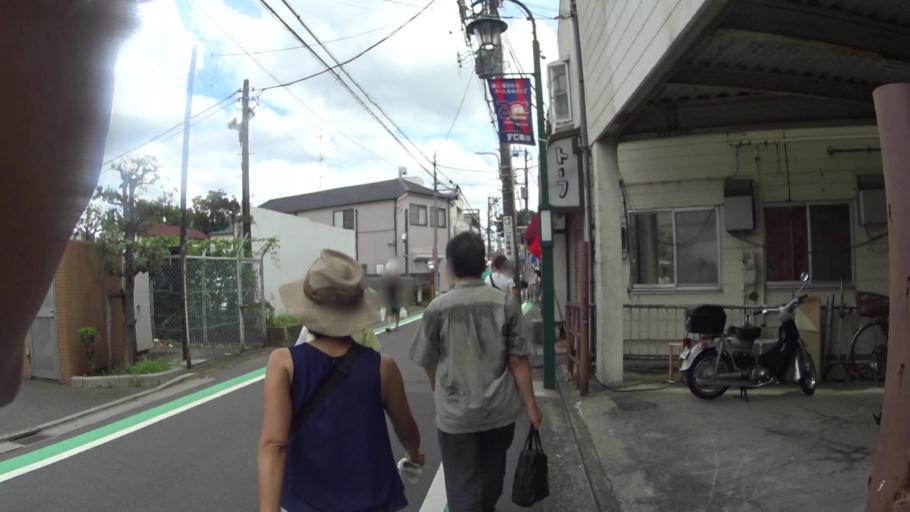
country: JP
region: Tokyo
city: Chofugaoka
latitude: 35.6567
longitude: 139.5657
